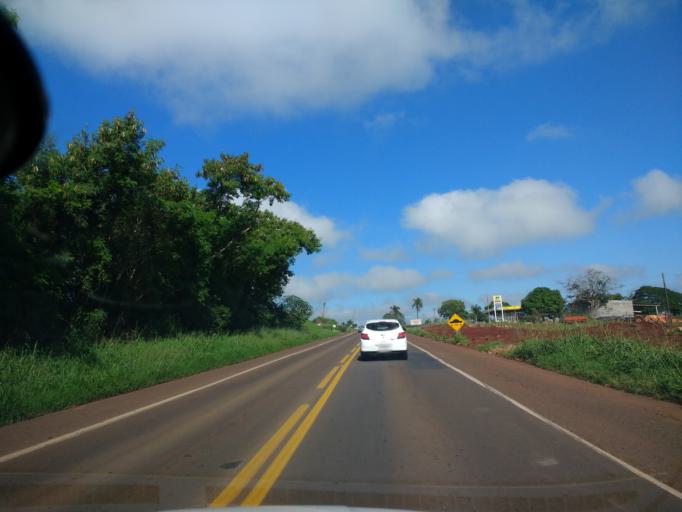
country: BR
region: Parana
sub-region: Paicandu
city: Paicandu
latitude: -23.5448
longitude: -52.2285
